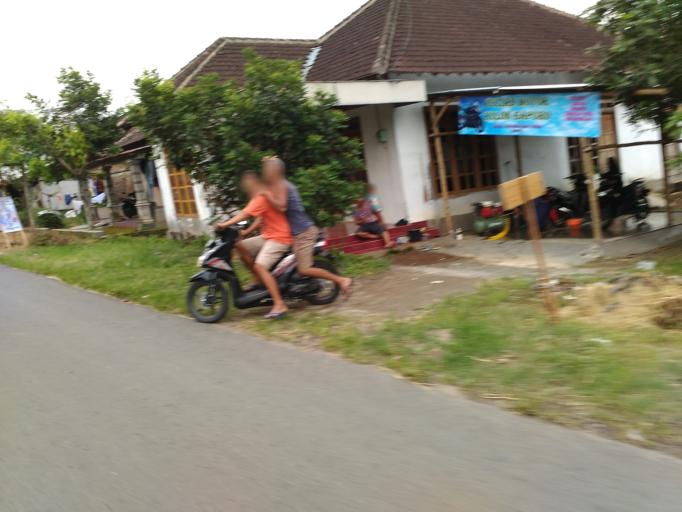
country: ID
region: Central Java
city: Delanggu
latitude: -7.5901
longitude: 110.6396
